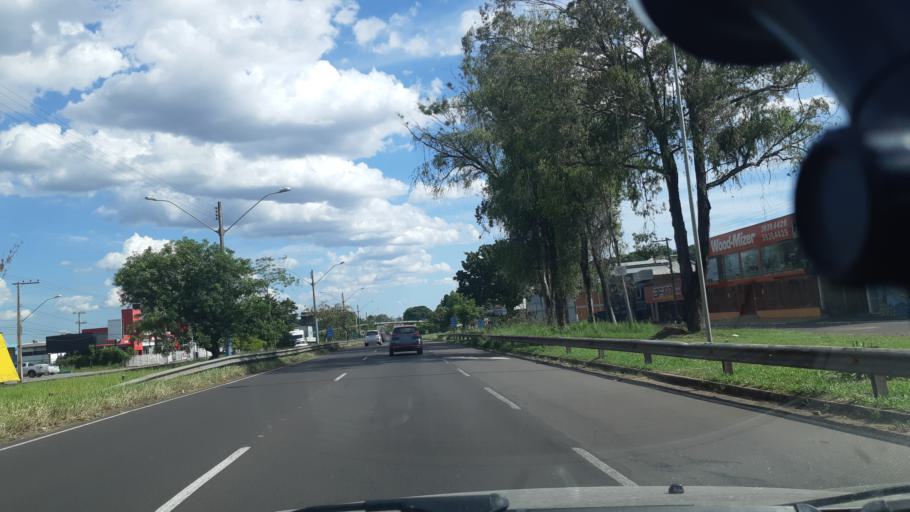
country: BR
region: Rio Grande do Sul
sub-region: Novo Hamburgo
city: Novo Hamburgo
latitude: -29.6742
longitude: -51.1428
